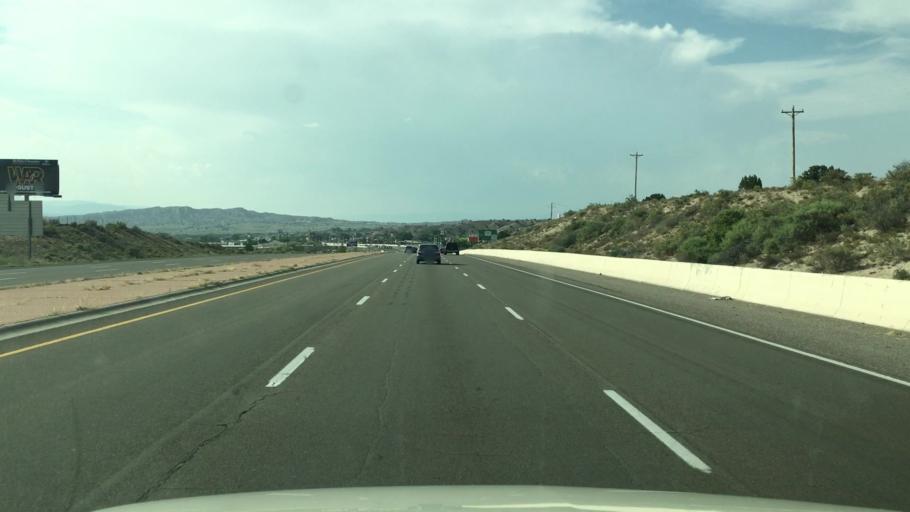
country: US
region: New Mexico
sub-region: Santa Fe County
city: Pojoaque
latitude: 35.8727
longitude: -106.0058
